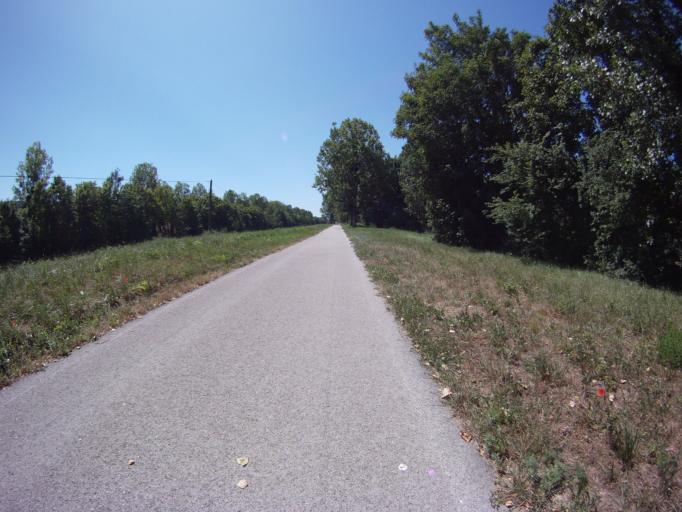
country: FR
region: Champagne-Ardenne
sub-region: Departement de la Marne
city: Damery
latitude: 49.0740
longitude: 3.8563
